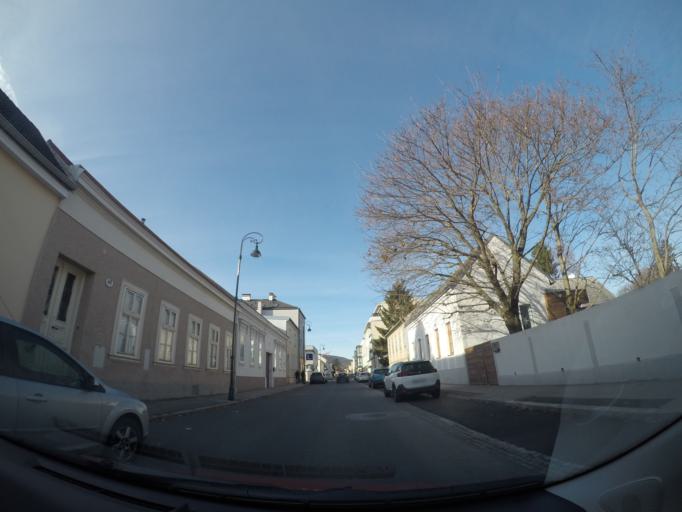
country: AT
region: Lower Austria
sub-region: Politischer Bezirk Baden
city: Baden
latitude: 48.0027
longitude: 16.2395
